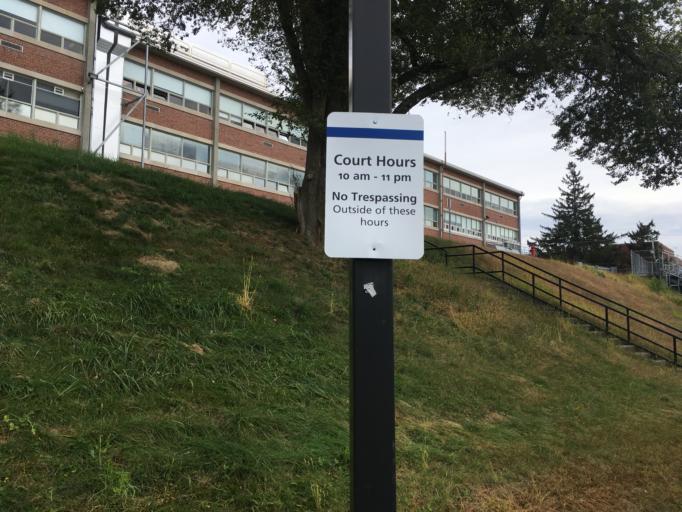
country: US
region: Massachusetts
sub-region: Middlesex County
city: Lowell
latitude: 42.6421
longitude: -71.3362
